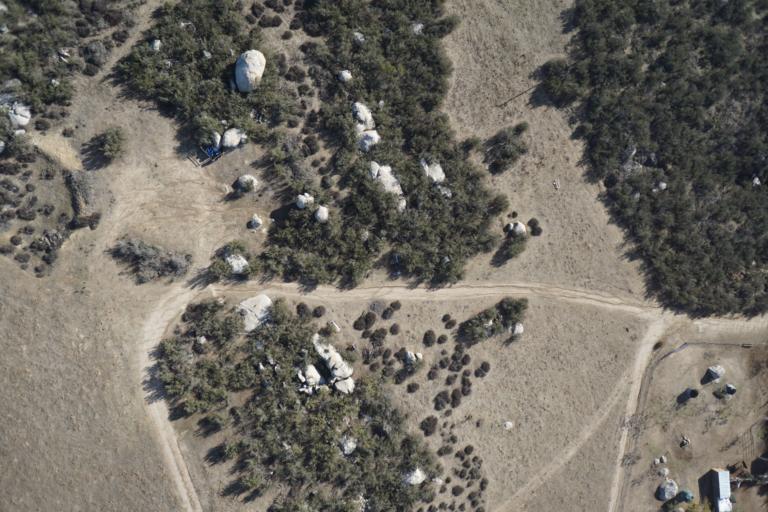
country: US
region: California
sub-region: Riverside County
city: East Hemet
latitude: 33.6254
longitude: -116.8976
